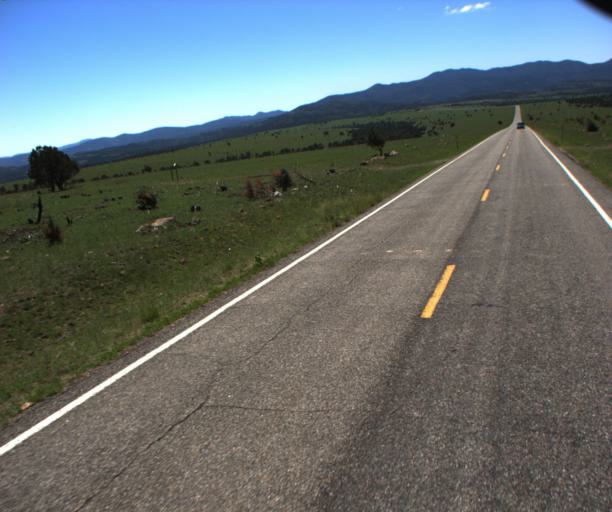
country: US
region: Arizona
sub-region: Greenlee County
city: Morenci
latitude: 33.3376
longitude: -109.3477
